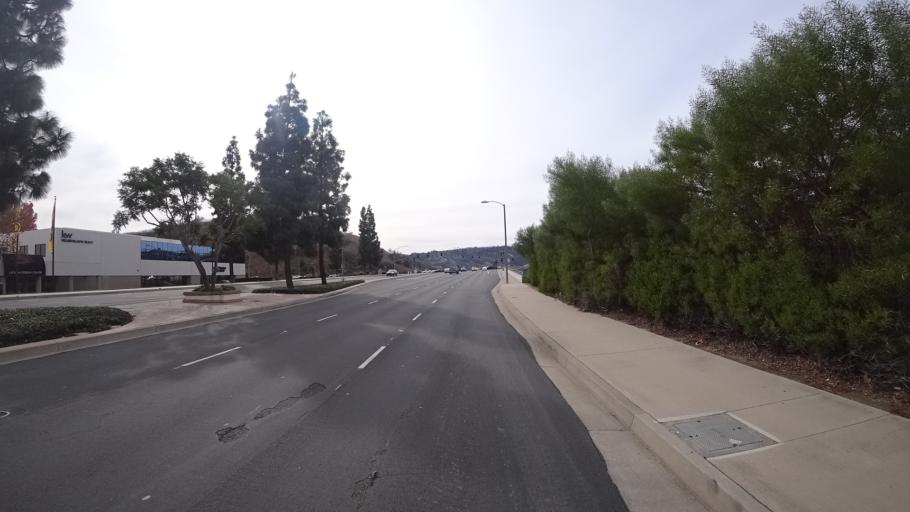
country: US
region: California
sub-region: Orange County
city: Aliso Viejo
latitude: 33.5570
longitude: -117.7173
